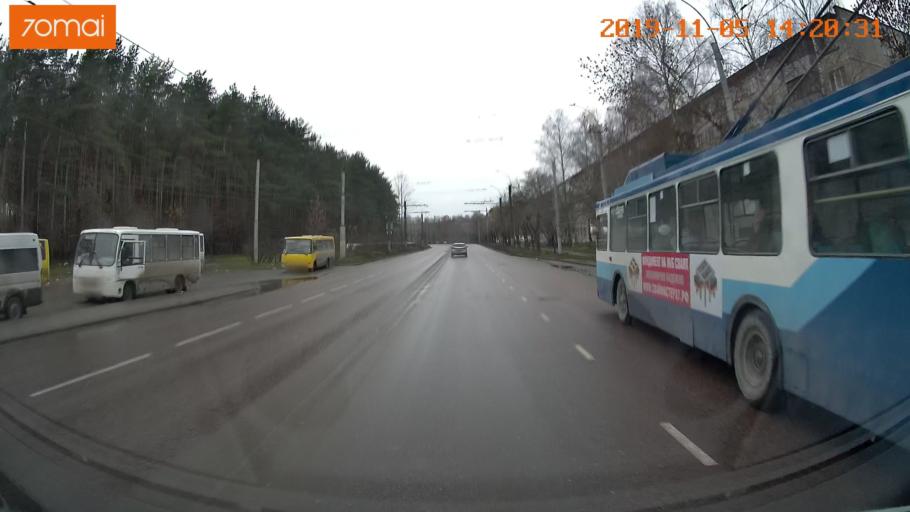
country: RU
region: Ivanovo
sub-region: Gorod Ivanovo
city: Ivanovo
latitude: 56.9578
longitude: 41.0209
